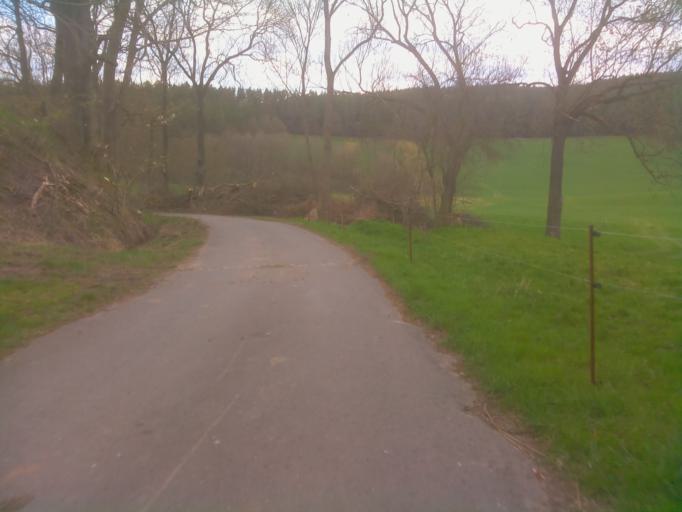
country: DE
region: Thuringia
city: Unterbodnitz
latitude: 50.8283
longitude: 11.6495
